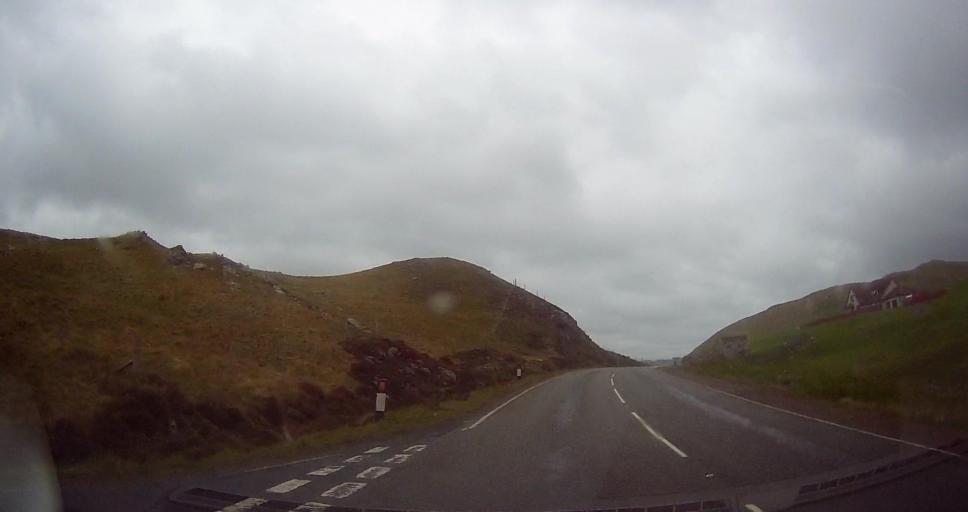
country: GB
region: Scotland
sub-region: Shetland Islands
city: Lerwick
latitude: 60.4062
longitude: -1.3870
